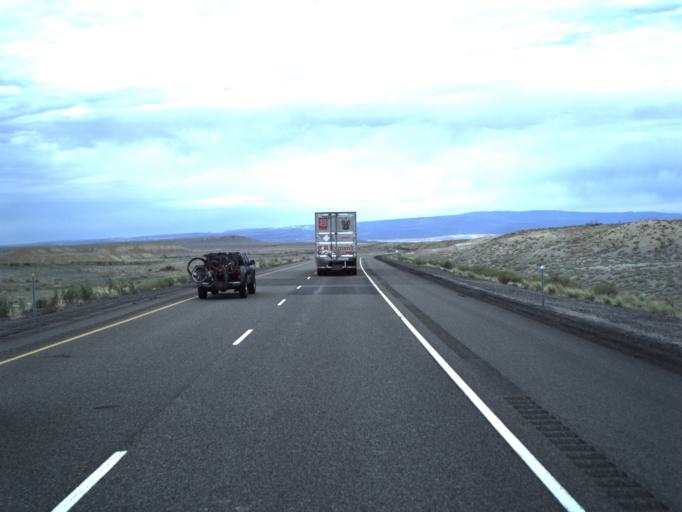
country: US
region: Utah
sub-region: Grand County
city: Moab
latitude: 38.9417
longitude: -109.5416
